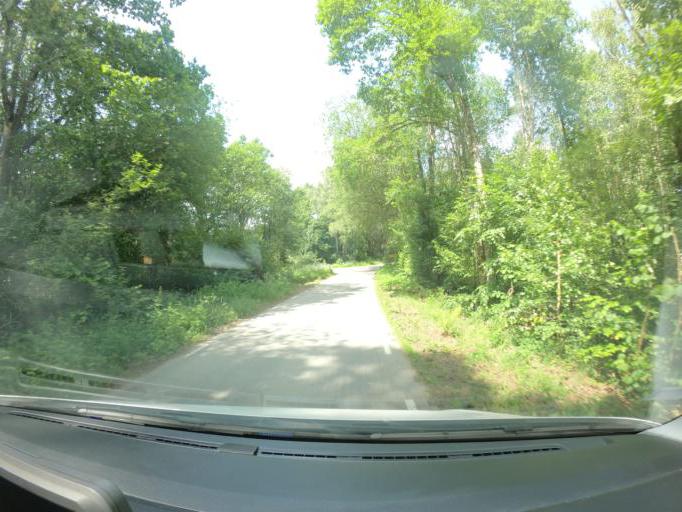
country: SE
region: Skane
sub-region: Hassleholms Kommun
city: Sosdala
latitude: 55.9601
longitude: 13.6412
